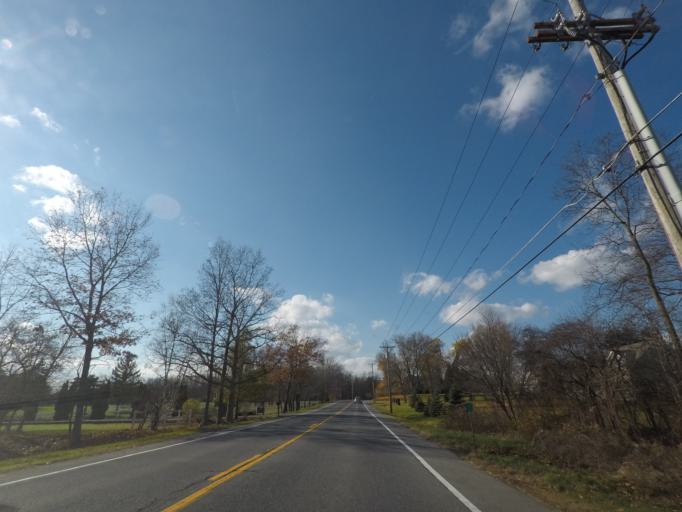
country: US
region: New York
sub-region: Saratoga County
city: Country Knolls
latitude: 42.8922
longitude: -73.8387
